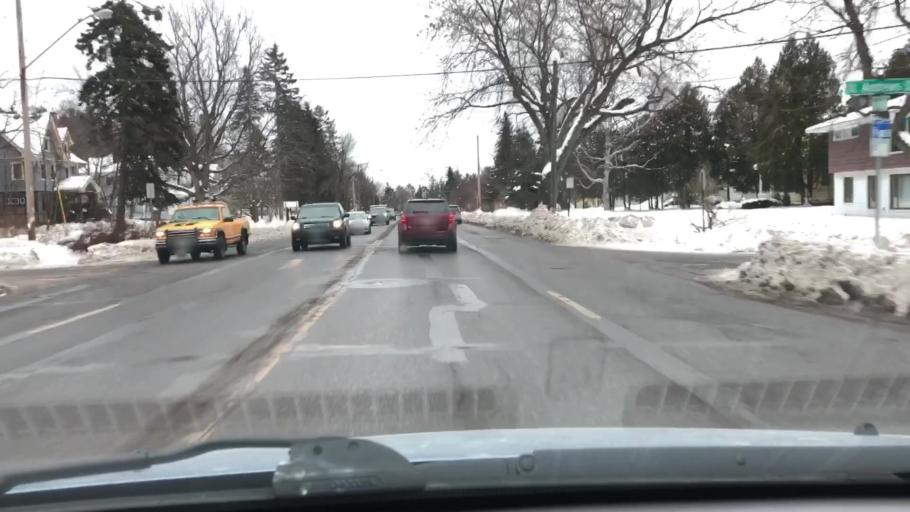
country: US
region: Minnesota
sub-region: Saint Louis County
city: Arnold
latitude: 46.8315
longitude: -92.0713
